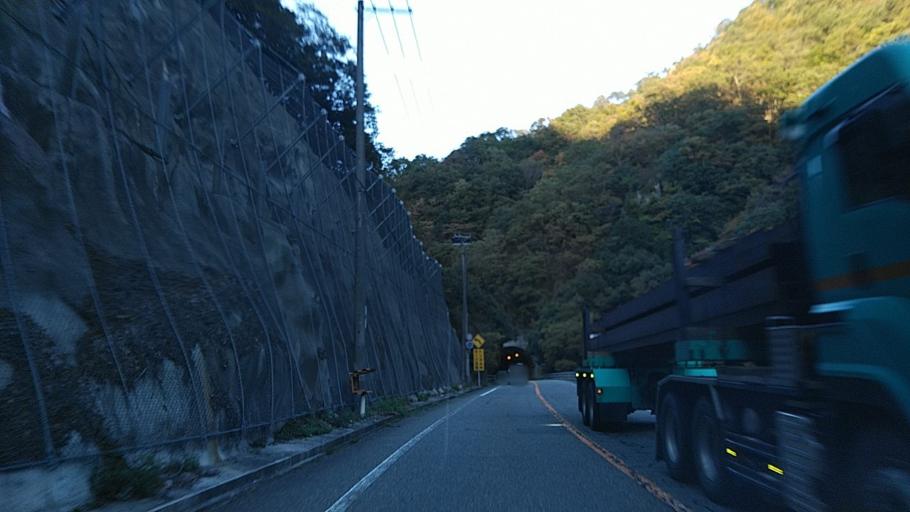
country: JP
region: Osaka
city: Ikeda
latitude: 34.9392
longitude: 135.4092
